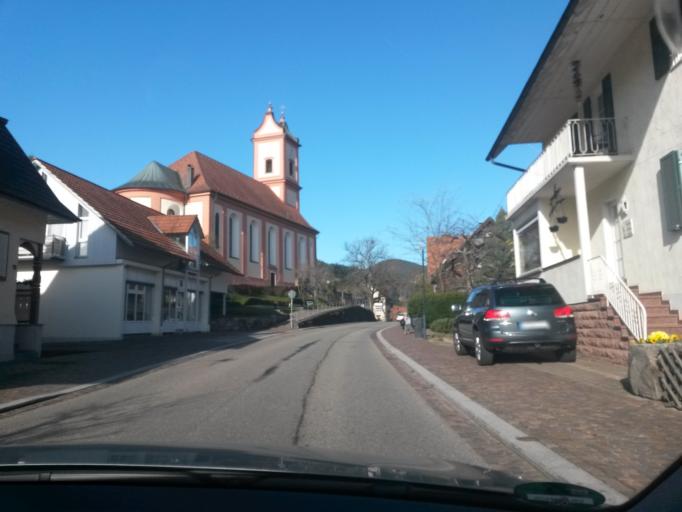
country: DE
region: Baden-Wuerttemberg
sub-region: Freiburg Region
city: Oberwolfach
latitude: 48.3160
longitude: 8.2173
